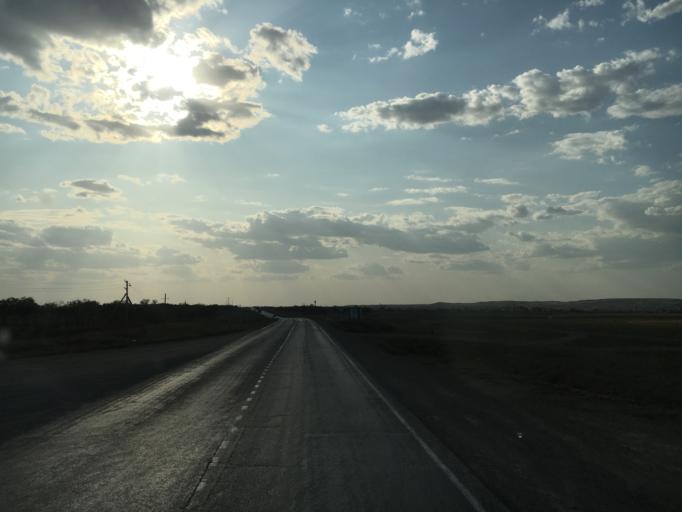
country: KZ
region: Aqtoebe
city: Aqtobe
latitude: 50.2941
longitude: 57.6072
